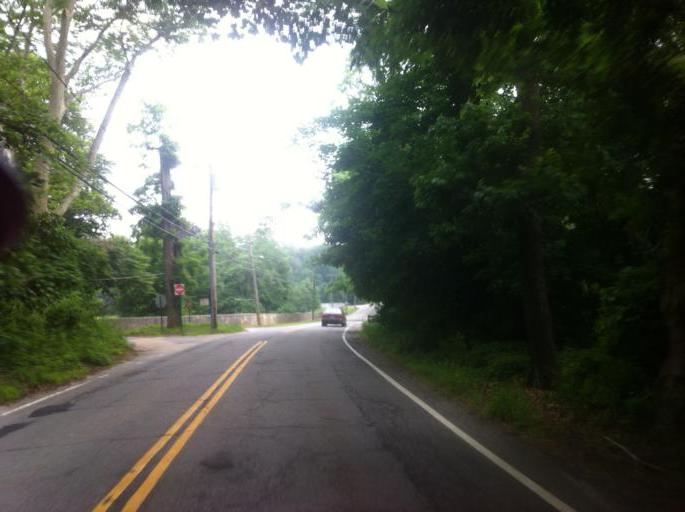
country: US
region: New York
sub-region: Nassau County
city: Upper Brookville
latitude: 40.8642
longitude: -73.5674
